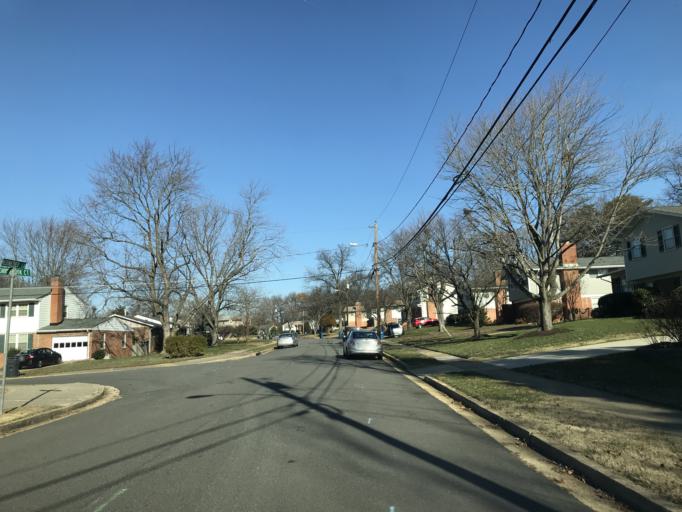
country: US
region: Virginia
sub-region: Fairfax County
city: Franconia
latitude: 38.7856
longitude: -77.1668
